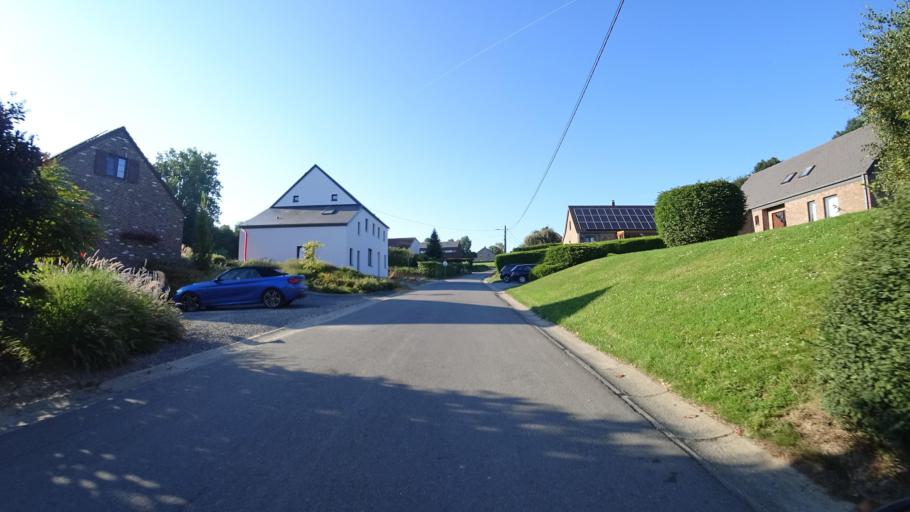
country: BE
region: Wallonia
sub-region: Province de Namur
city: Namur
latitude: 50.5172
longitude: 4.8395
